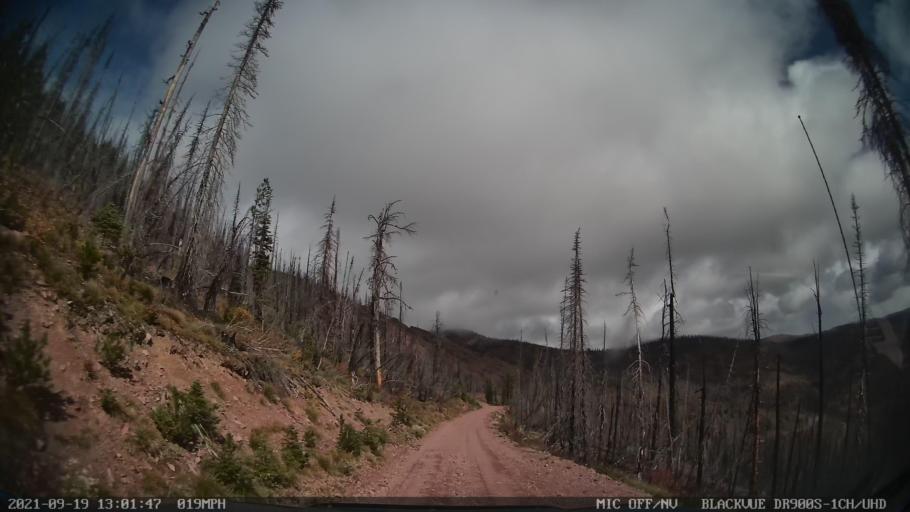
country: US
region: Montana
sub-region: Missoula County
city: Seeley Lake
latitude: 47.1871
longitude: -113.3545
